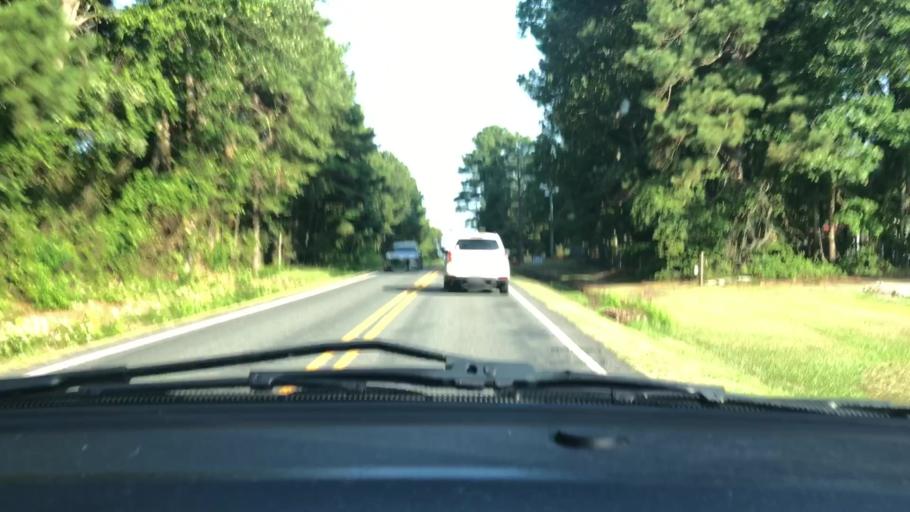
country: US
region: North Carolina
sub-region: Lee County
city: Broadway
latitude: 35.3707
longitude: -79.0981
